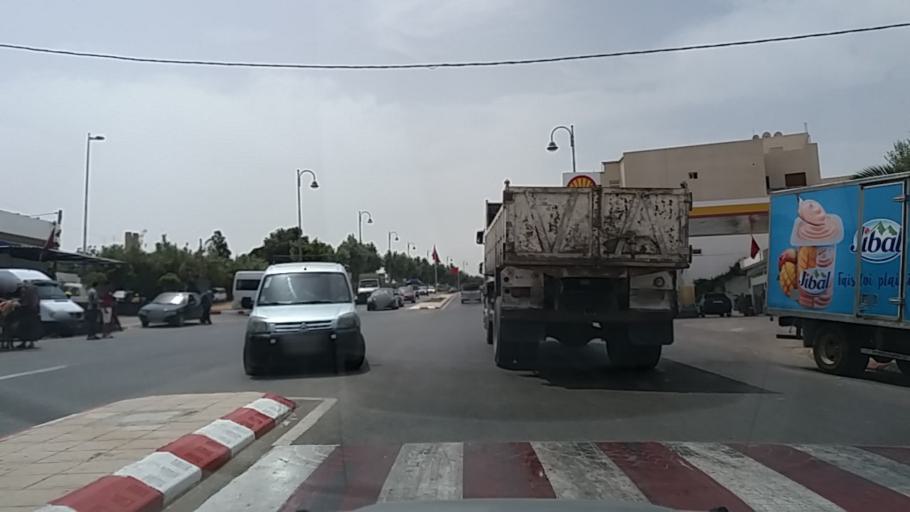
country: MA
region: Tanger-Tetouan
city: Asilah
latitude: 35.4642
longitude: -6.0307
